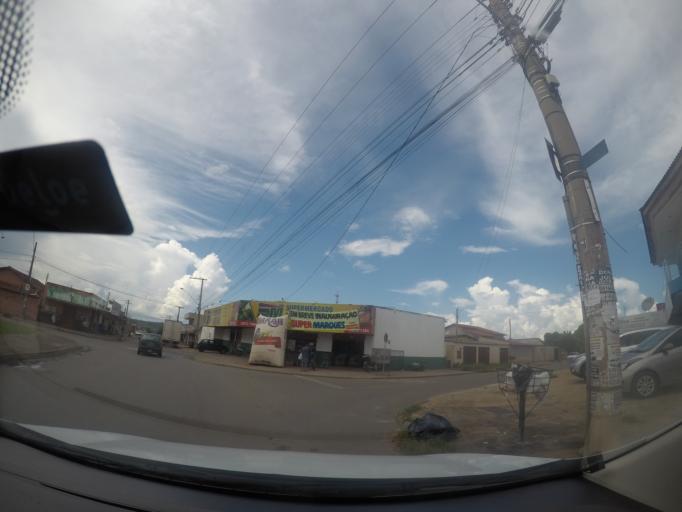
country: BR
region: Goias
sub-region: Goiania
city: Goiania
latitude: -16.7037
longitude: -49.3571
